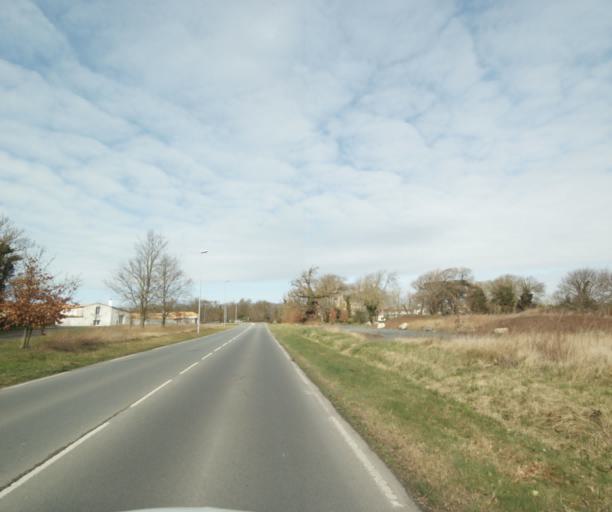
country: FR
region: Poitou-Charentes
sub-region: Departement de la Charente-Maritime
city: Lagord
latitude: 46.1830
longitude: -1.1738
